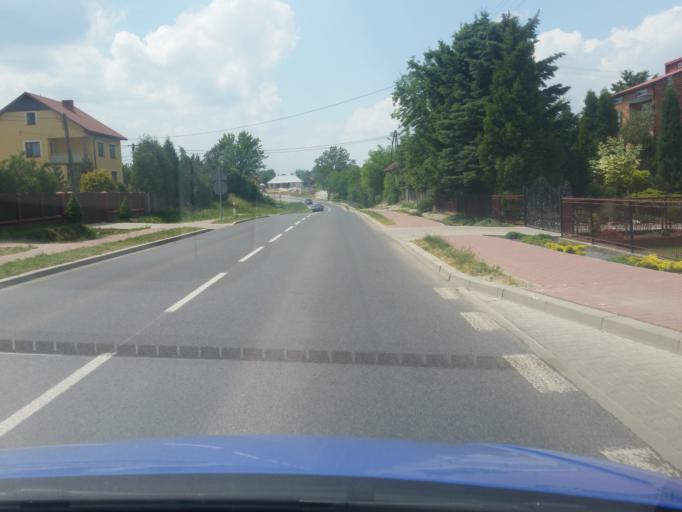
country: PL
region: Swietokrzyskie
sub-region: Powiat pinczowski
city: Zlota
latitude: 50.3382
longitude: 20.6121
